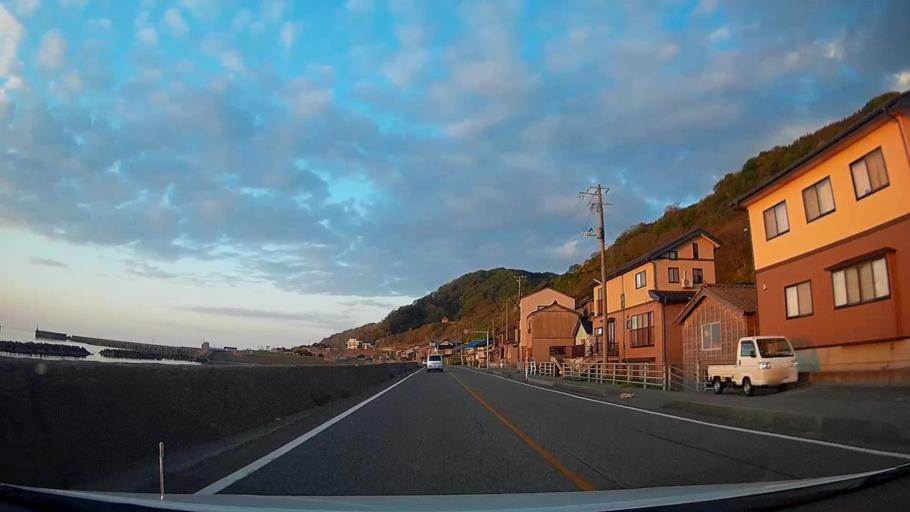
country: JP
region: Niigata
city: Joetsu
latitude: 37.1285
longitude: 138.0495
